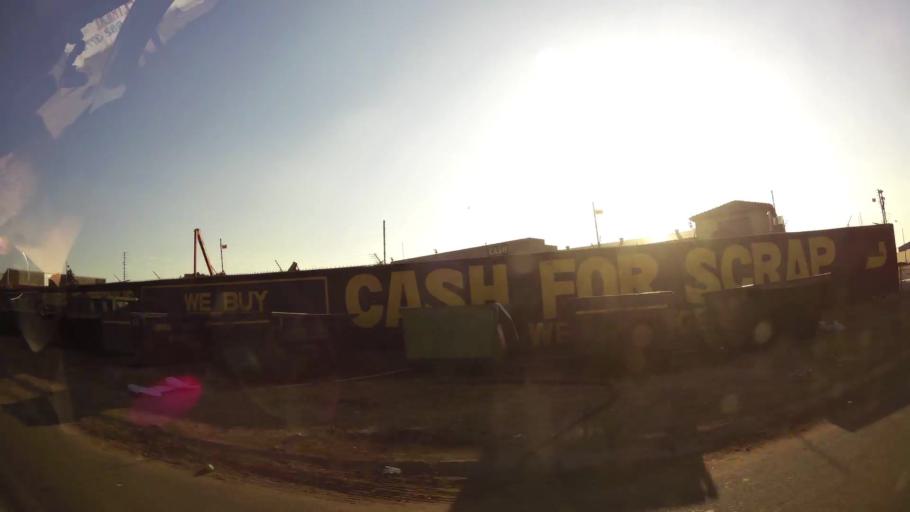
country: ZA
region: Gauteng
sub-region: West Rand District Municipality
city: Randfontein
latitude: -26.2018
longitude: 27.6958
